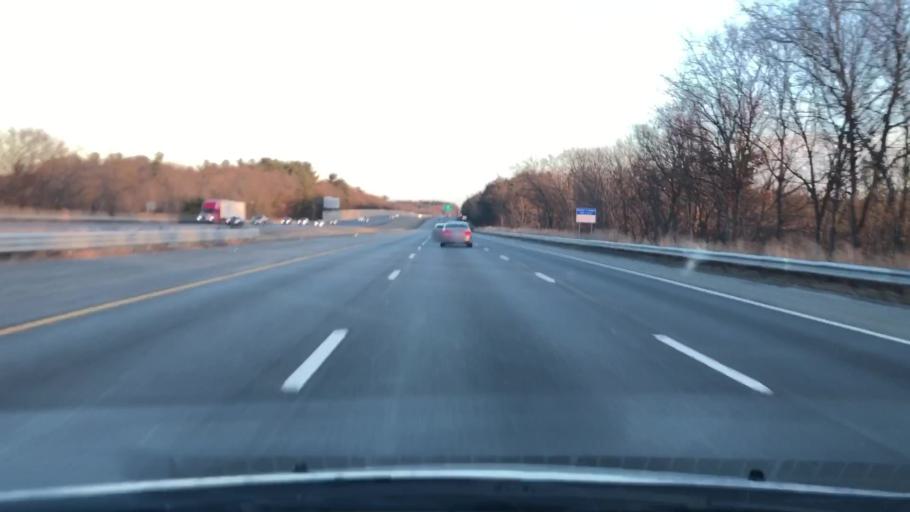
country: US
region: Massachusetts
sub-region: Middlesex County
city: Chelmsford
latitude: 42.6266
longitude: -71.3898
